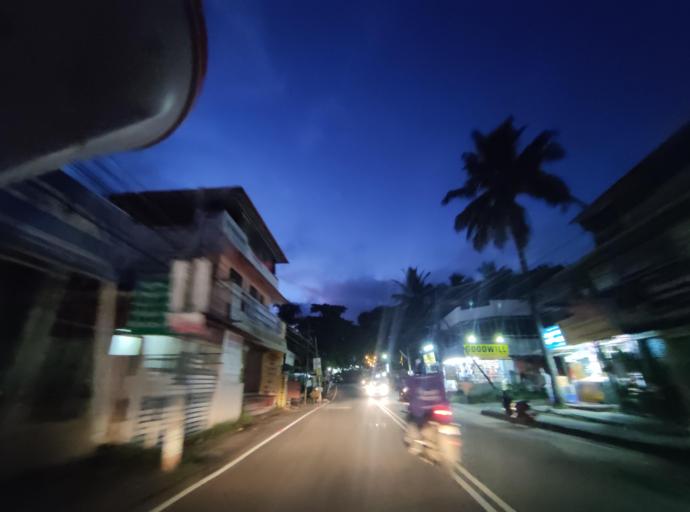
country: IN
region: Kerala
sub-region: Thiruvananthapuram
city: Nedumangad
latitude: 8.5513
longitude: 76.9609
